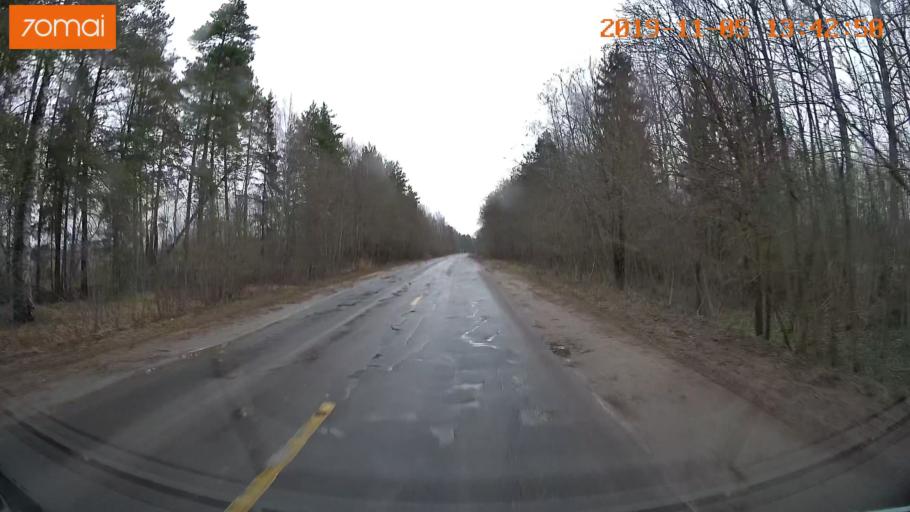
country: RU
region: Ivanovo
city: Shuya
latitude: 56.9693
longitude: 41.3982
